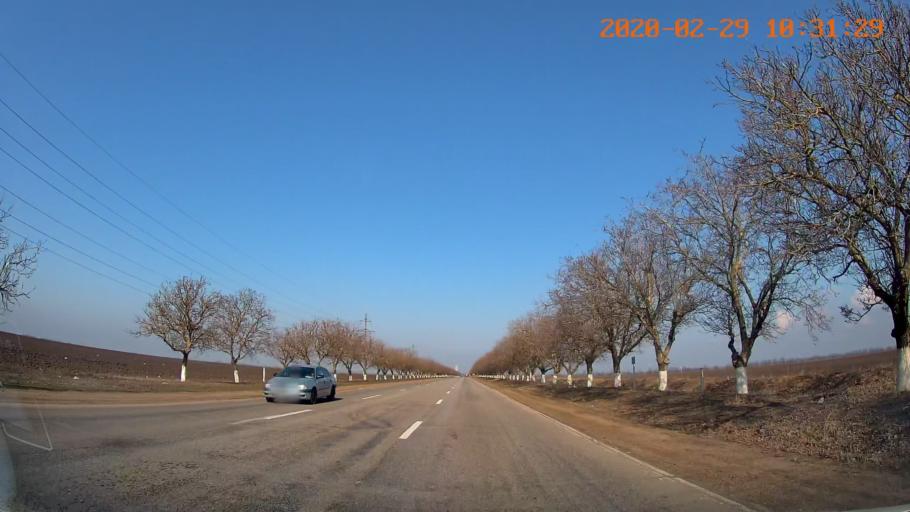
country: MD
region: Telenesti
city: Tiraspolul Nou
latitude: 46.9489
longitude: 29.5635
